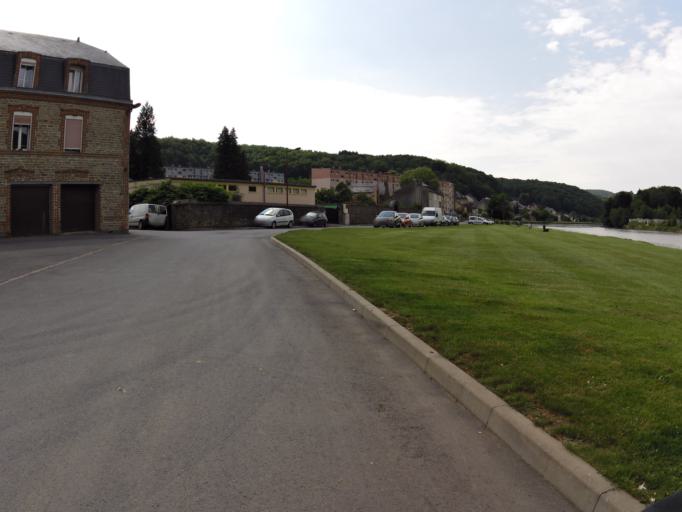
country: FR
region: Champagne-Ardenne
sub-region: Departement des Ardennes
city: Nouzonville
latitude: 49.8525
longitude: 4.7684
